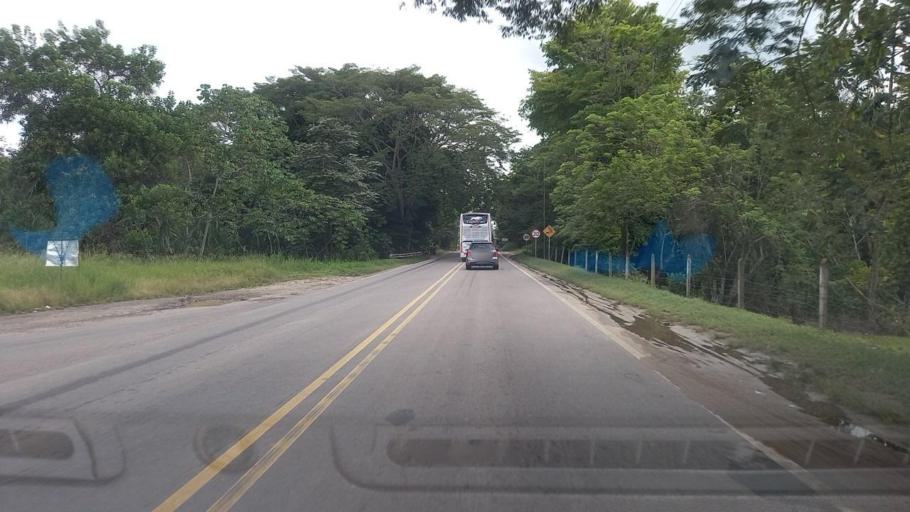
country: CO
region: Santander
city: Barrancabermeja
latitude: 7.1237
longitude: -73.5866
